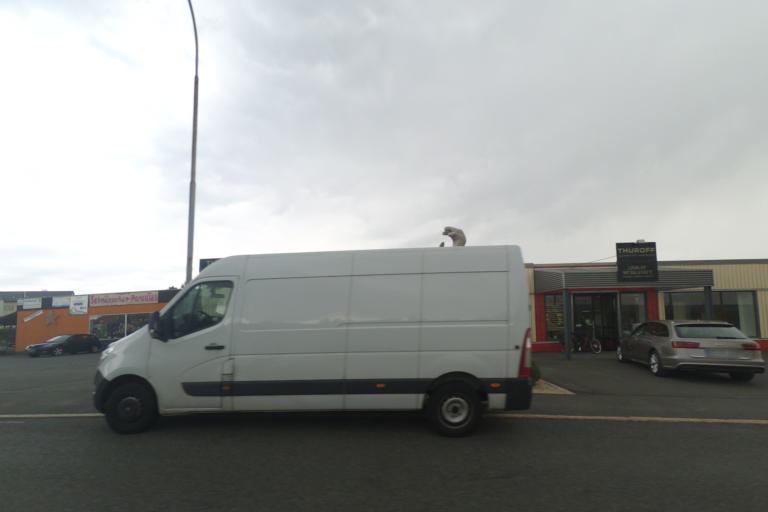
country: DE
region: Bavaria
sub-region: Upper Franconia
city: Helmbrechts
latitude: 50.2334
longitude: 11.7262
